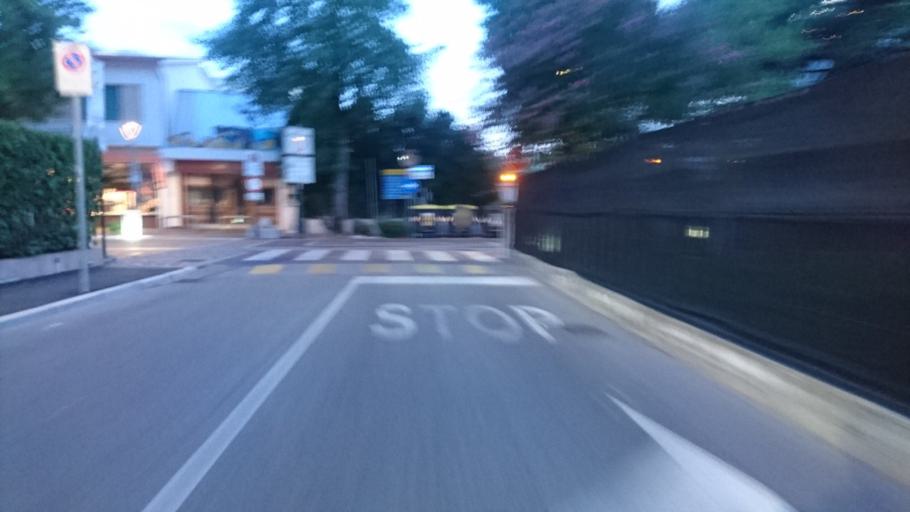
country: IT
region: Veneto
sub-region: Provincia di Padova
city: Abano Terme
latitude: 45.3538
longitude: 11.7783
